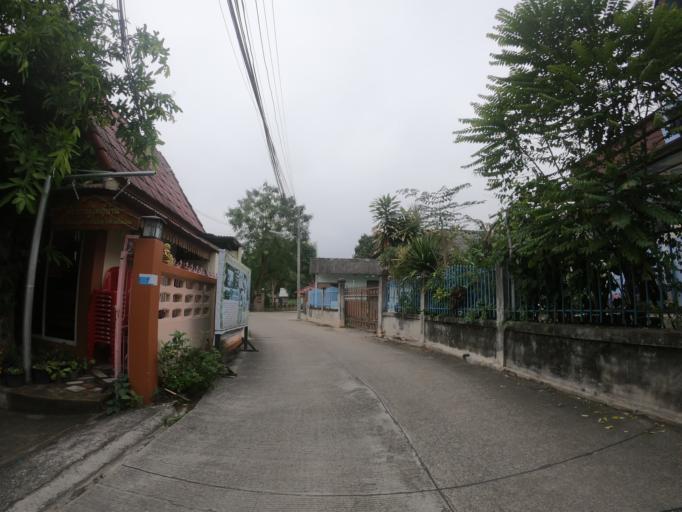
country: TH
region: Chiang Mai
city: Hang Dong
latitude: 18.7366
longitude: 98.9536
